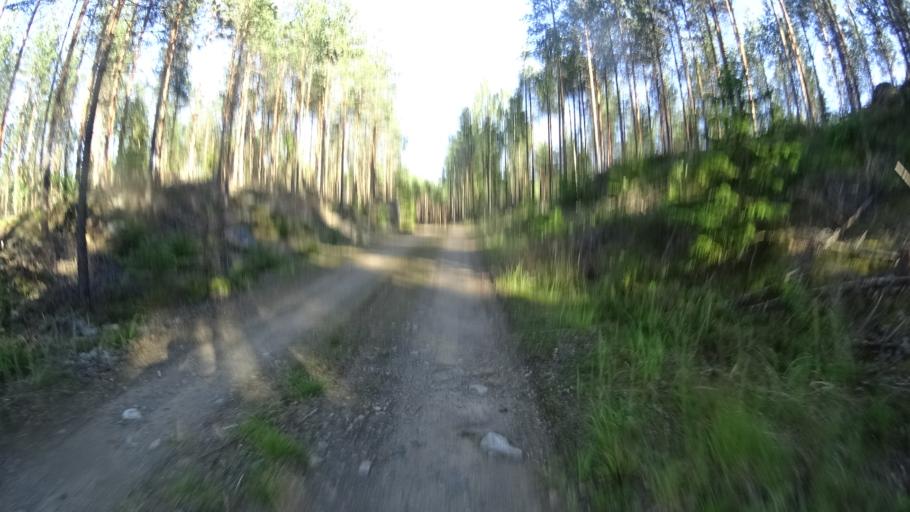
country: FI
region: Uusimaa
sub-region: Helsinki
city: Karkkila
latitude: 60.6649
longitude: 24.1307
